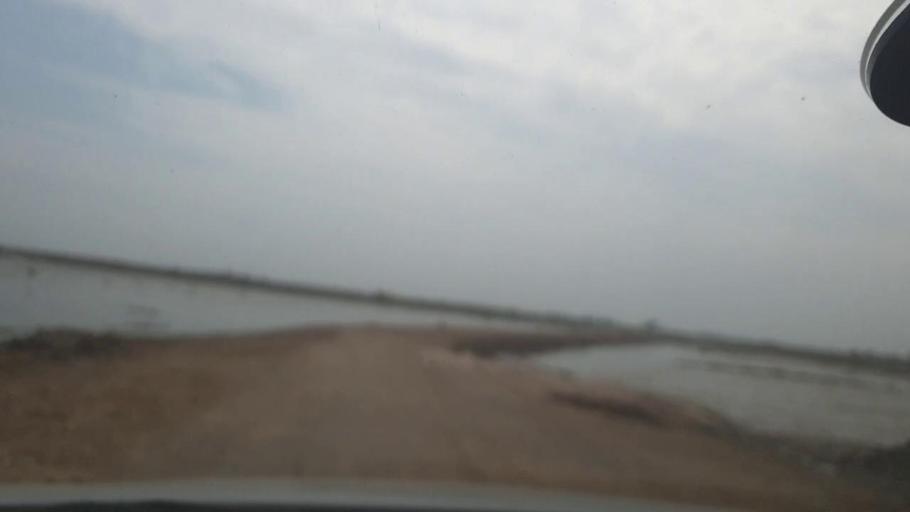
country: PK
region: Balochistan
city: Garhi Khairo
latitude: 28.0154
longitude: 68.0435
